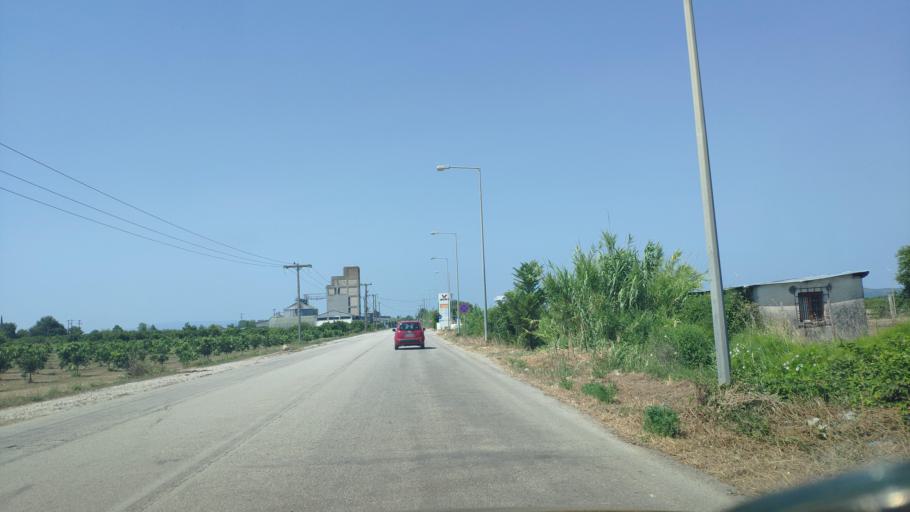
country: GR
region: Epirus
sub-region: Nomos Artas
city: Kostakioi
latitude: 39.1306
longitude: 20.9494
